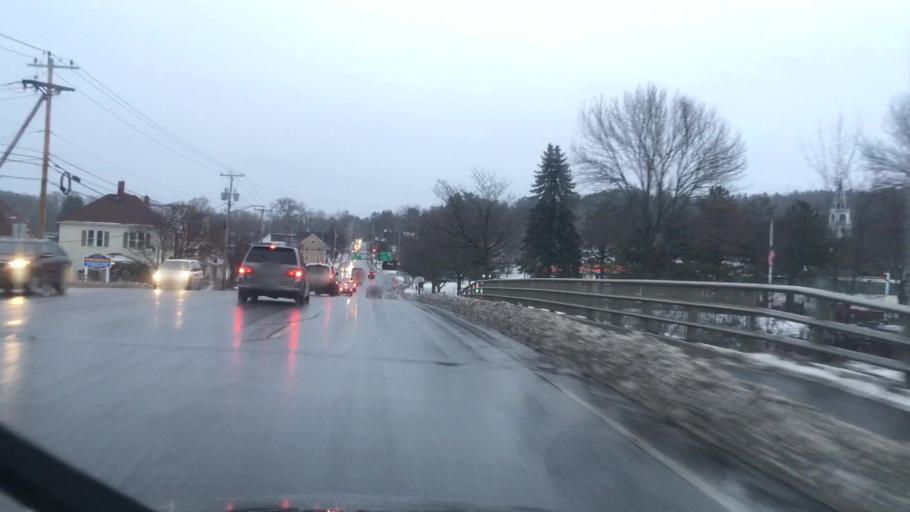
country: US
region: New Hampshire
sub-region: Sullivan County
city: Newport
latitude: 43.3613
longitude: -72.1741
